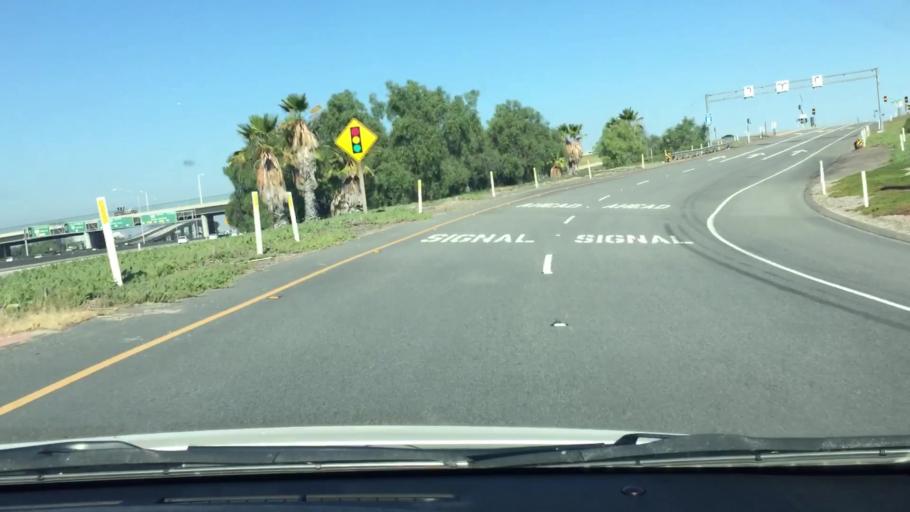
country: US
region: California
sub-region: Orange County
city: Laguna Woods
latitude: 33.6367
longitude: -117.7278
